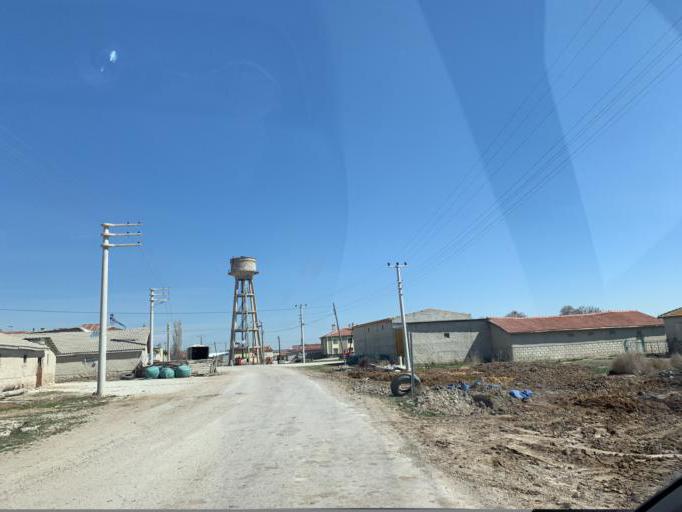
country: TR
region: Konya
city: Yarma
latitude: 37.7508
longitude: 32.8585
